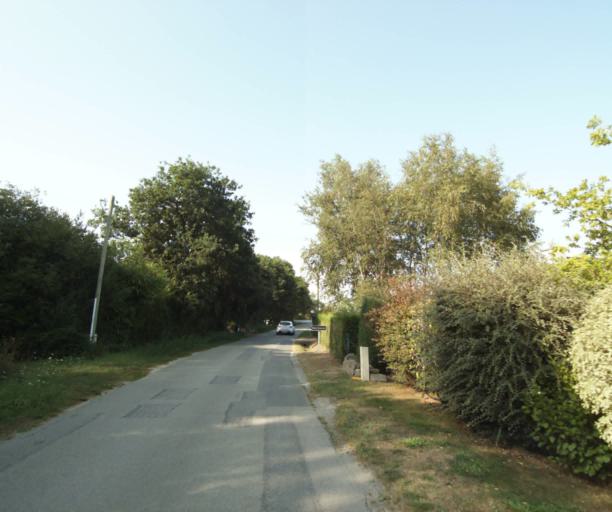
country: FR
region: Brittany
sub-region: Departement du Morbihan
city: Riantec
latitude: 47.7371
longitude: -3.2956
